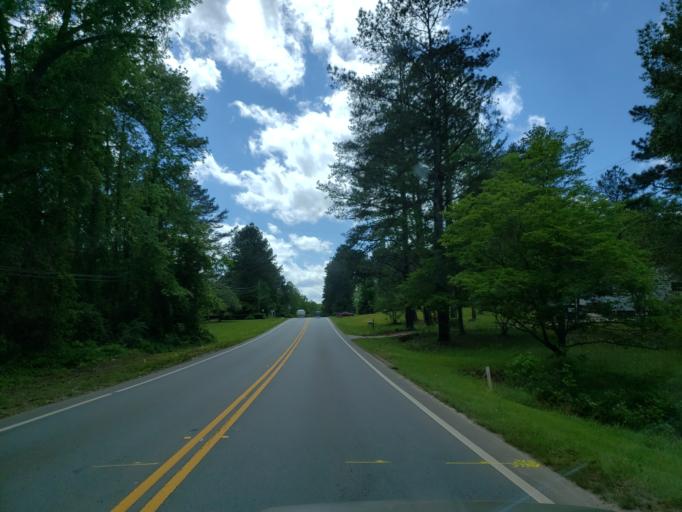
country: US
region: Georgia
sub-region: Haralson County
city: Bremen
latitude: 33.7231
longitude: -85.0906
